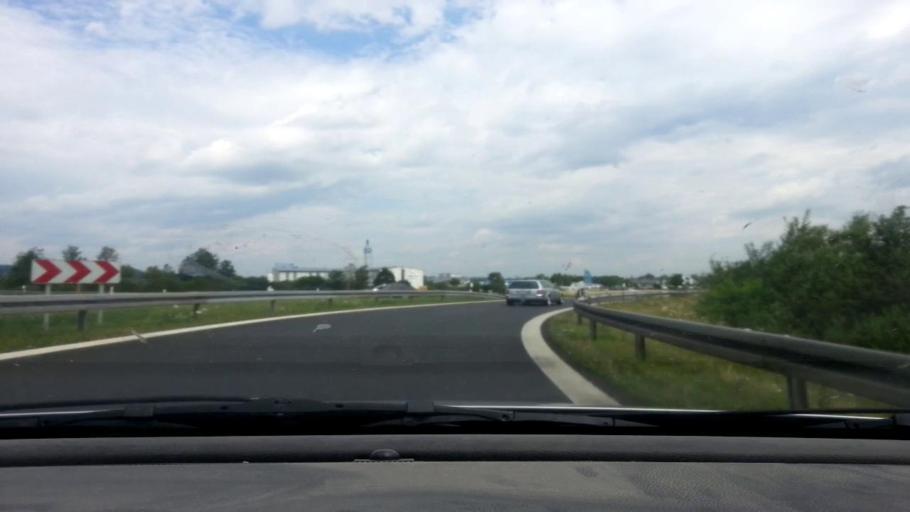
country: DE
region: Bavaria
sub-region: Upper Palatinate
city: Mitterteich
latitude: 49.9344
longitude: 12.2257
